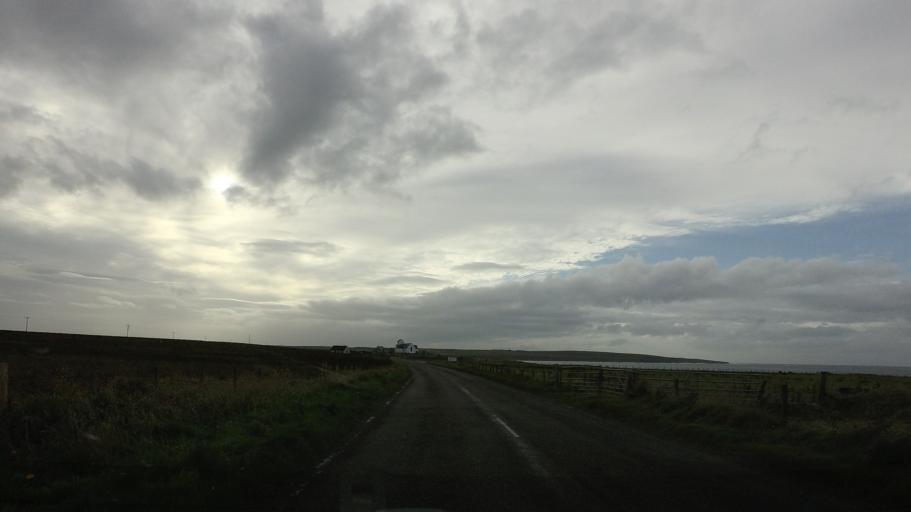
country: GB
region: Scotland
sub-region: Highland
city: Wick
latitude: 58.6385
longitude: -3.1256
